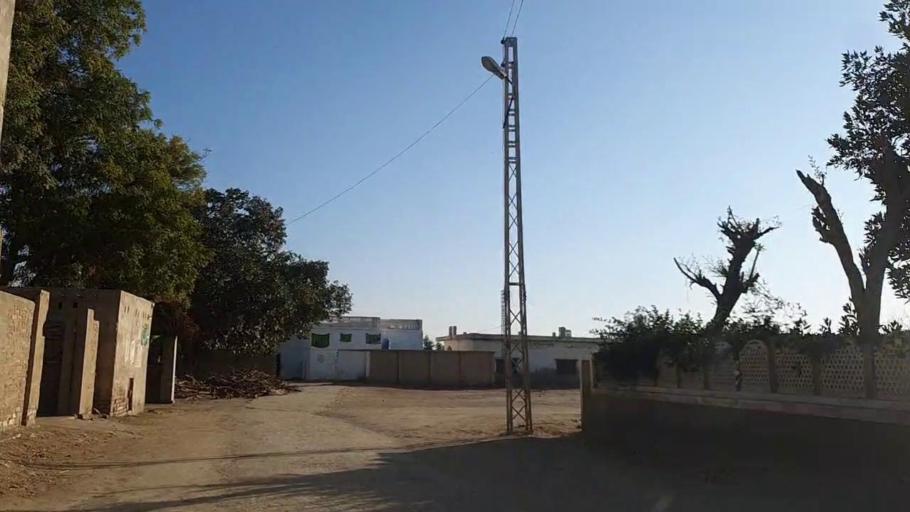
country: PK
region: Sindh
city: Samaro
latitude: 25.3382
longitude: 69.3976
